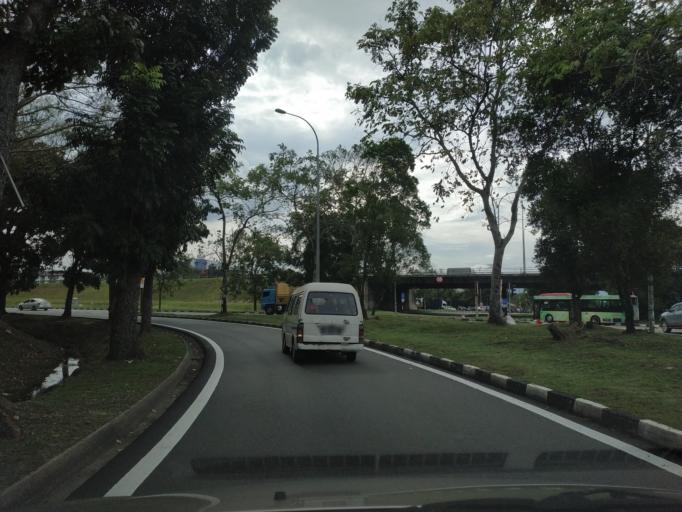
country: MY
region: Penang
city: Perai
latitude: 5.3990
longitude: 100.4073
